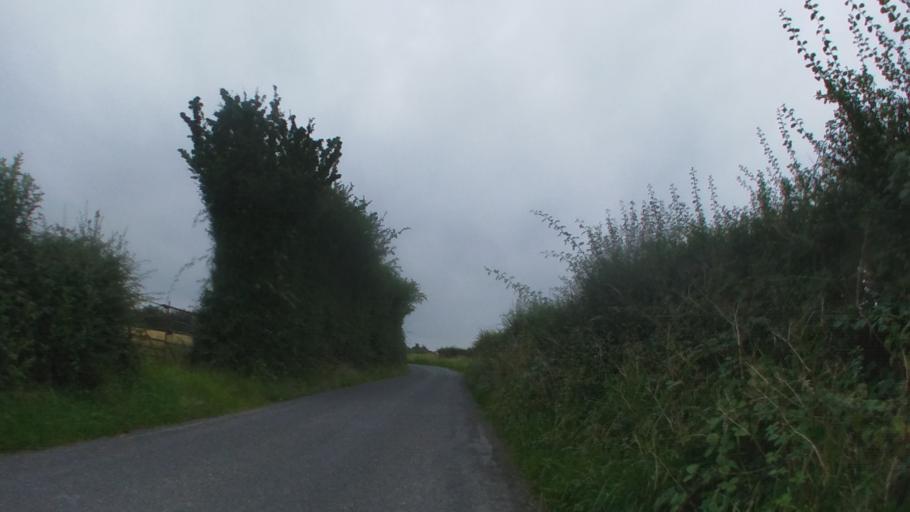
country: IE
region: Leinster
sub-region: Kilkenny
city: Kilkenny
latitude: 52.6988
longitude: -7.1985
